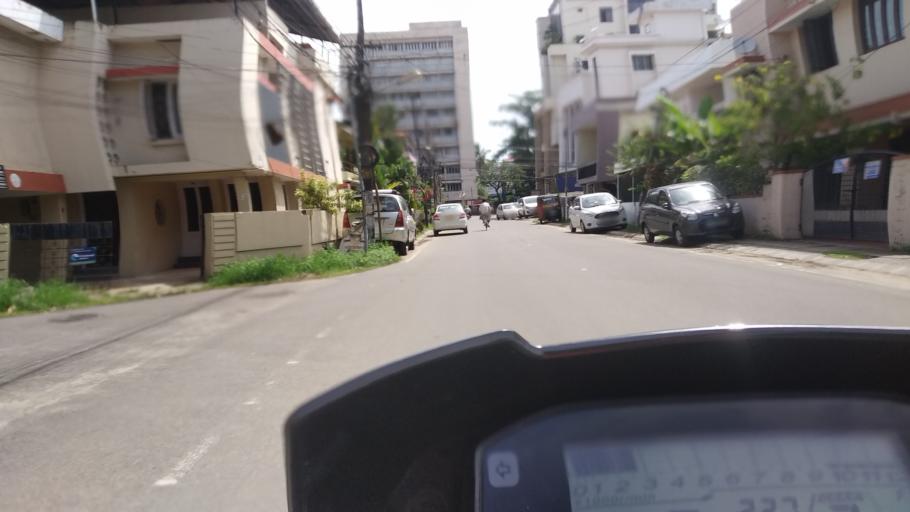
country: IN
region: Kerala
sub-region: Ernakulam
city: Cochin
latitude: 9.9650
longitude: 76.2959
